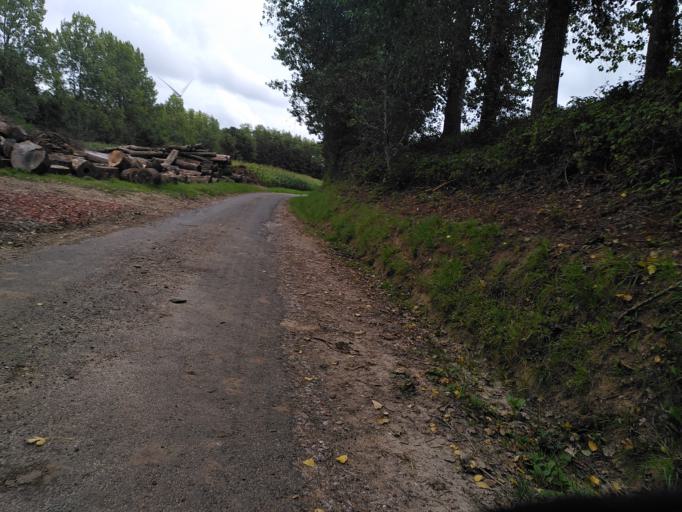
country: FR
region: Nord-Pas-de-Calais
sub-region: Departement du Pas-de-Calais
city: Lumbres
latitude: 50.6110
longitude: 2.1169
